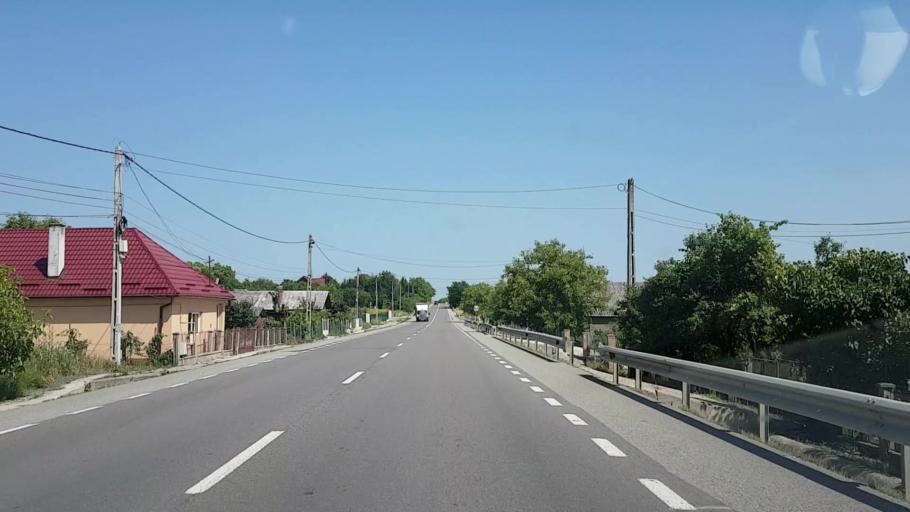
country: RO
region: Bistrita-Nasaud
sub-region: Comuna Uriu
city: Cristestii Ciceului
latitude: 47.1861
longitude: 24.1216
